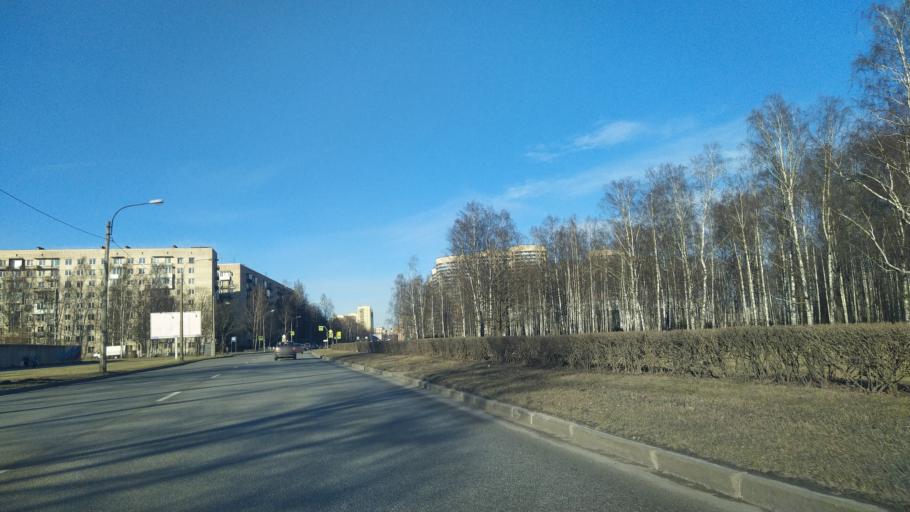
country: RU
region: Leningrad
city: Kalininskiy
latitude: 59.9986
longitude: 30.3938
